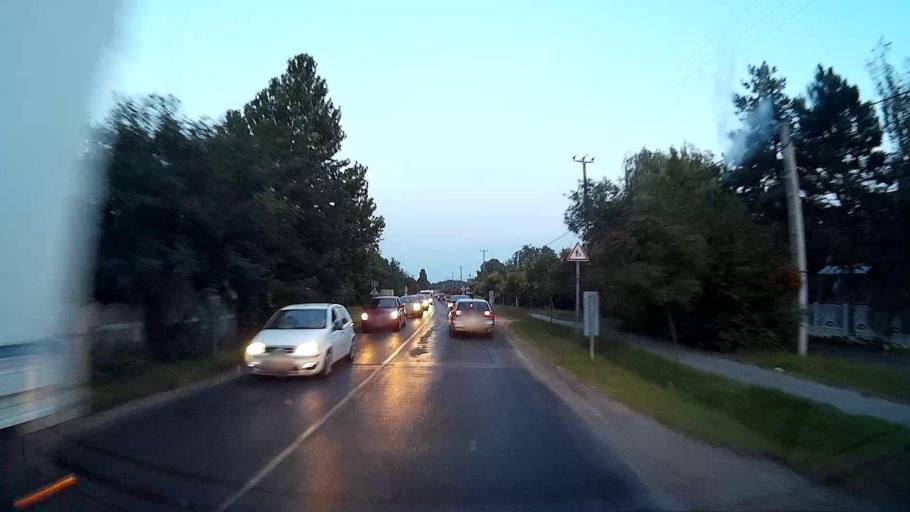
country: HU
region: Pest
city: Cegledbercel
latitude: 47.2114
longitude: 19.6812
